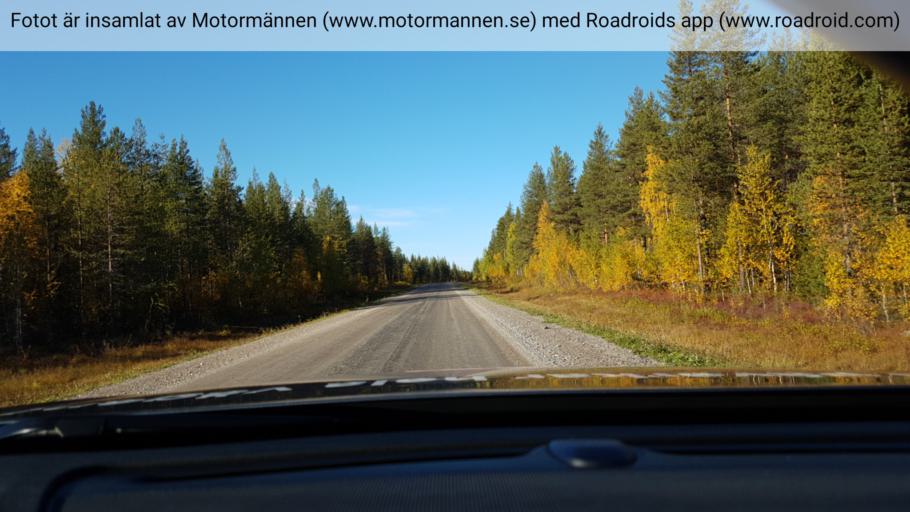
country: SE
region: Norrbotten
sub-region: Alvsbyns Kommun
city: AElvsbyn
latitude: 66.2651
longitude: 21.0495
